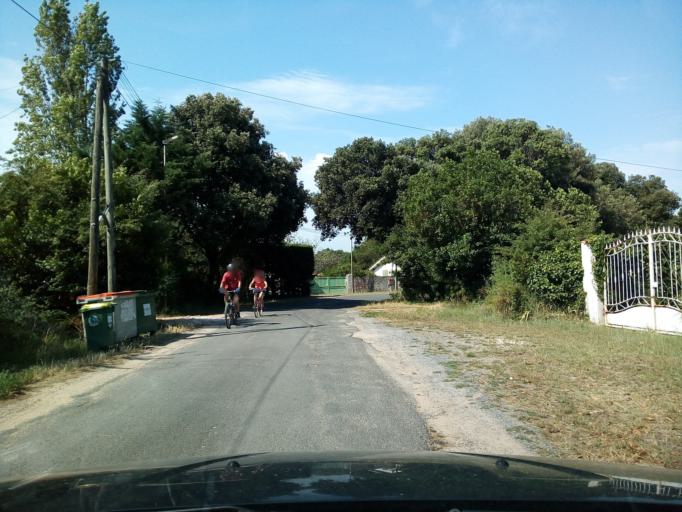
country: FR
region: Poitou-Charentes
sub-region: Departement de la Charente-Maritime
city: Boyard-Ville
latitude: 45.9570
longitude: -1.2579
